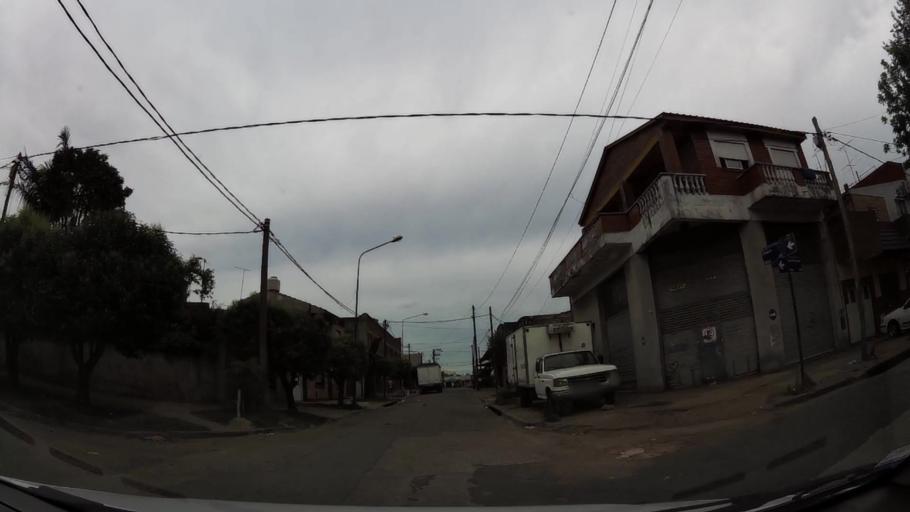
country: AR
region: Buenos Aires
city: San Justo
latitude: -34.6644
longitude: -58.5192
